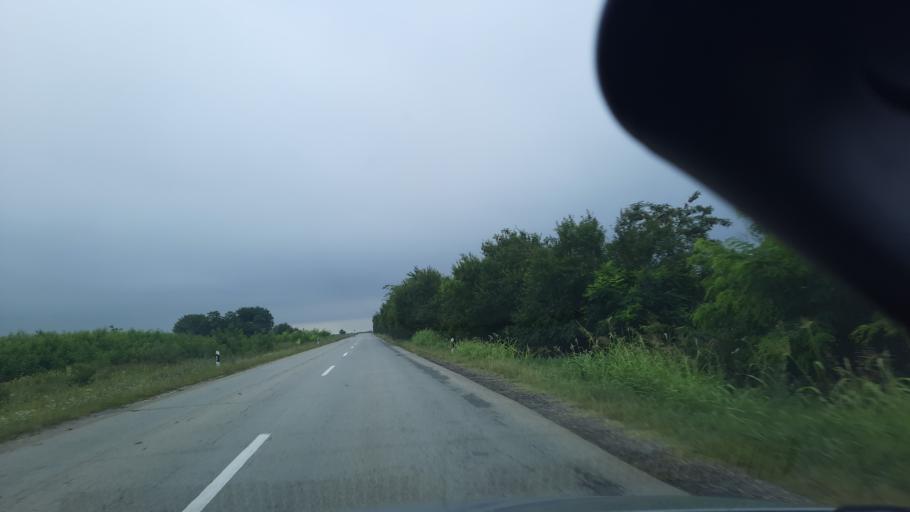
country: RS
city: Perlez
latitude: 45.2026
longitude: 20.4058
